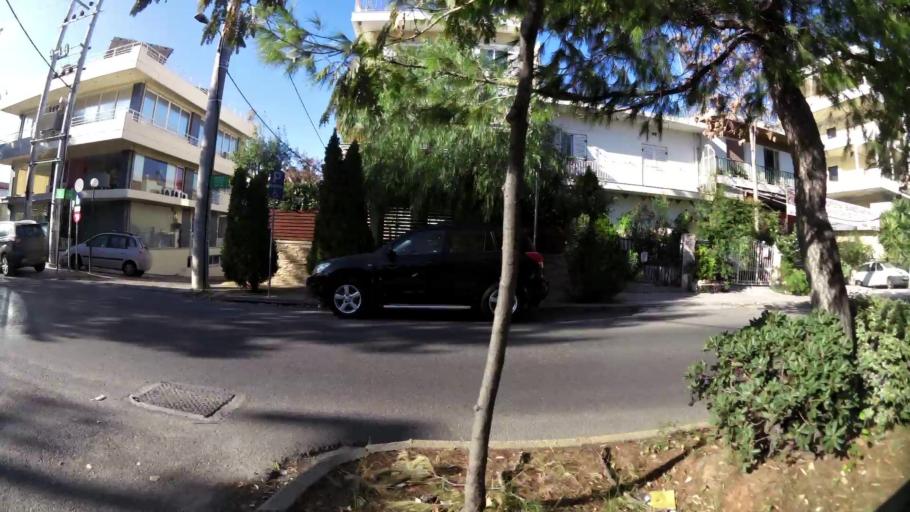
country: GR
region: Attica
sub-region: Nomarchia Athinas
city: Lykovrysi
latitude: 38.0553
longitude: 23.7796
